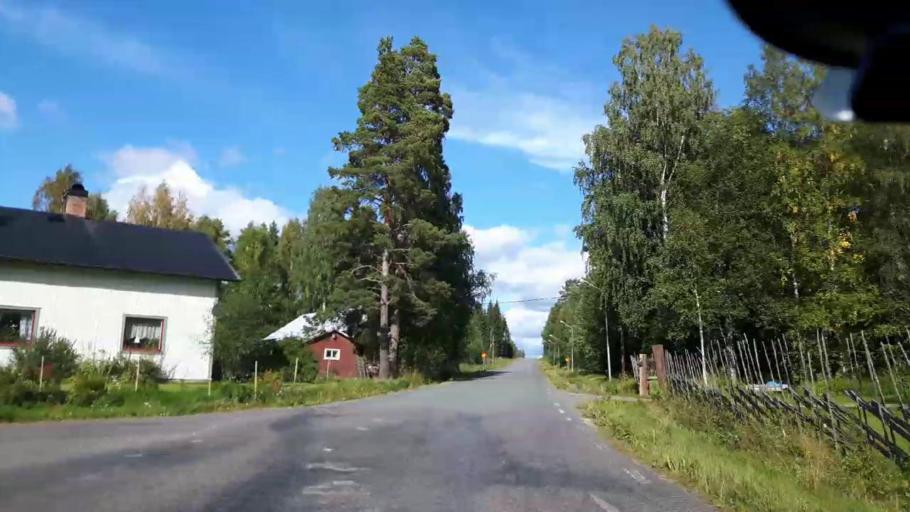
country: SE
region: Jaemtland
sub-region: Braecke Kommun
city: Braecke
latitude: 63.1809
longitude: 15.5547
